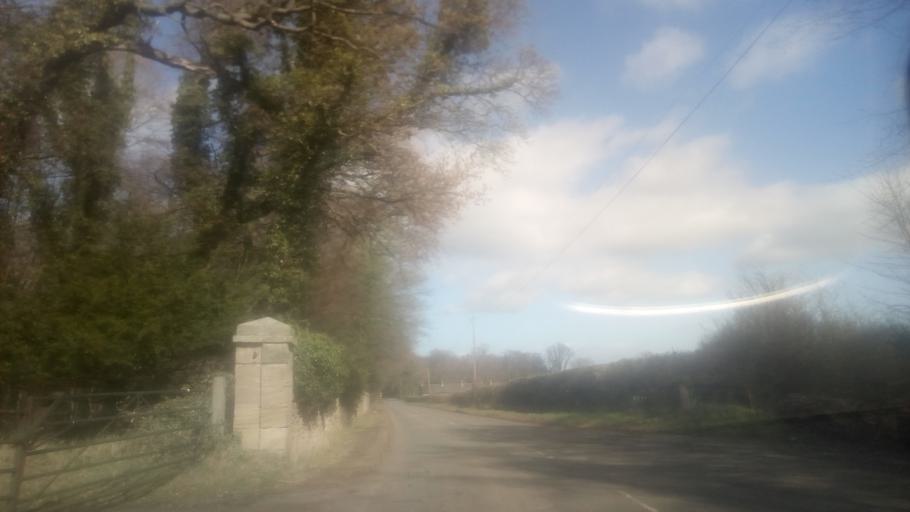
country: GB
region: Scotland
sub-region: Fife
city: Pathhead
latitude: 55.8793
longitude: -2.9608
